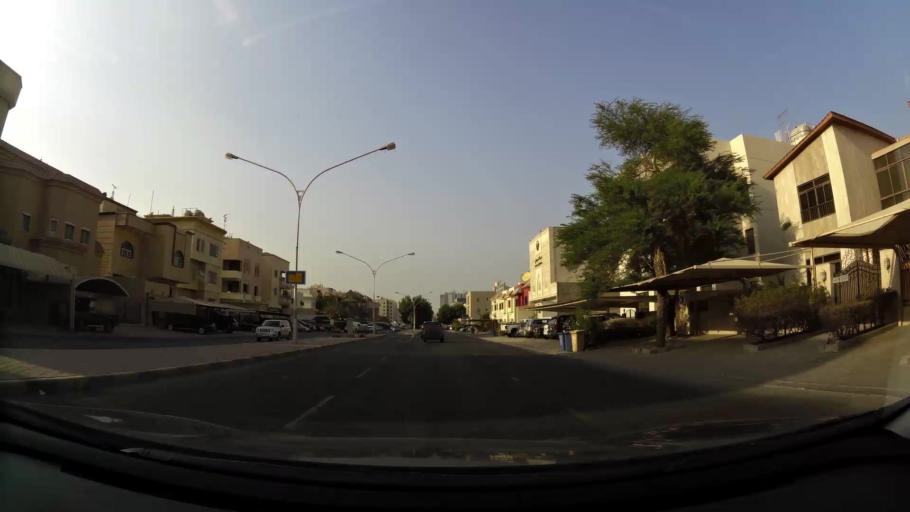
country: KW
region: Muhafazat Hawalli
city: Hawalli
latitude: 29.3194
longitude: 48.0329
